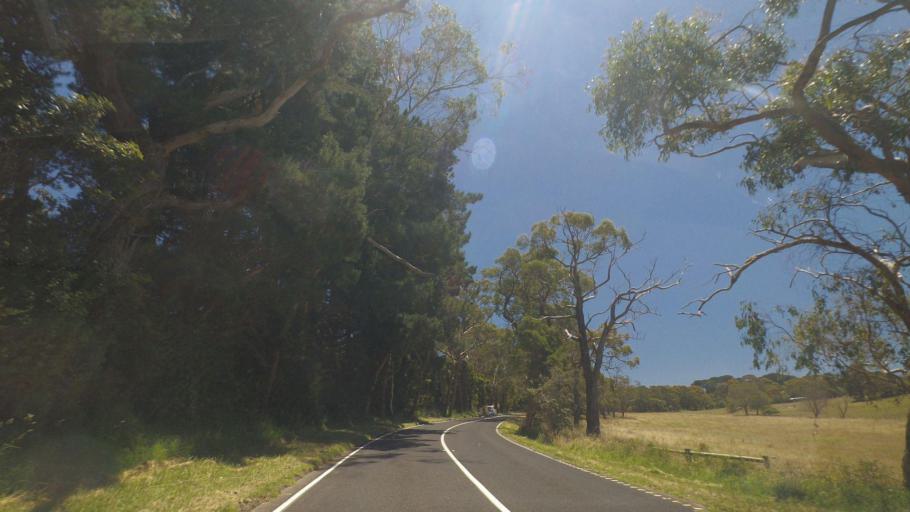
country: AU
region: Victoria
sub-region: Mornington Peninsula
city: McCrae
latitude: -38.4019
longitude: 144.9563
